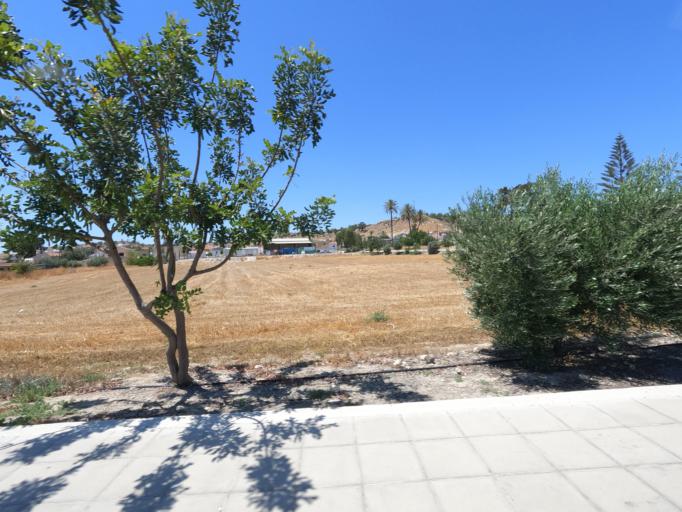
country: CY
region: Larnaka
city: Pyla
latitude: 35.0135
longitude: 33.6951
